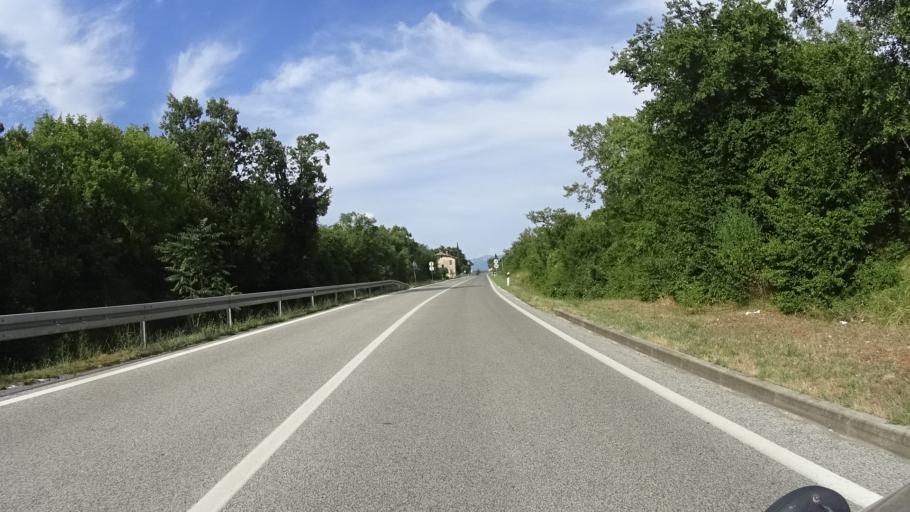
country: HR
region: Istarska
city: Rasa
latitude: 45.0493
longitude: 14.0093
